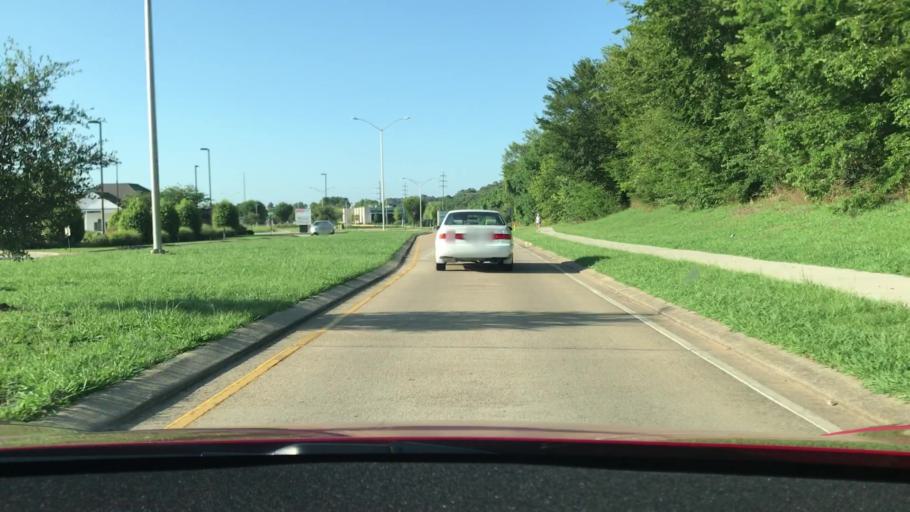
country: US
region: Louisiana
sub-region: Bossier Parish
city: Bossier City
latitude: 32.4481
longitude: -93.7309
